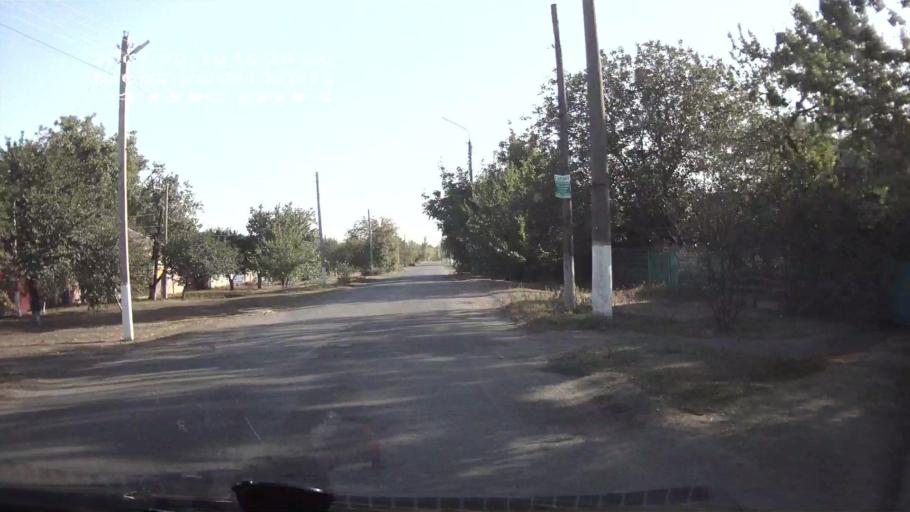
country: RU
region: Rostov
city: Gigant
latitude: 46.5214
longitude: 41.1911
